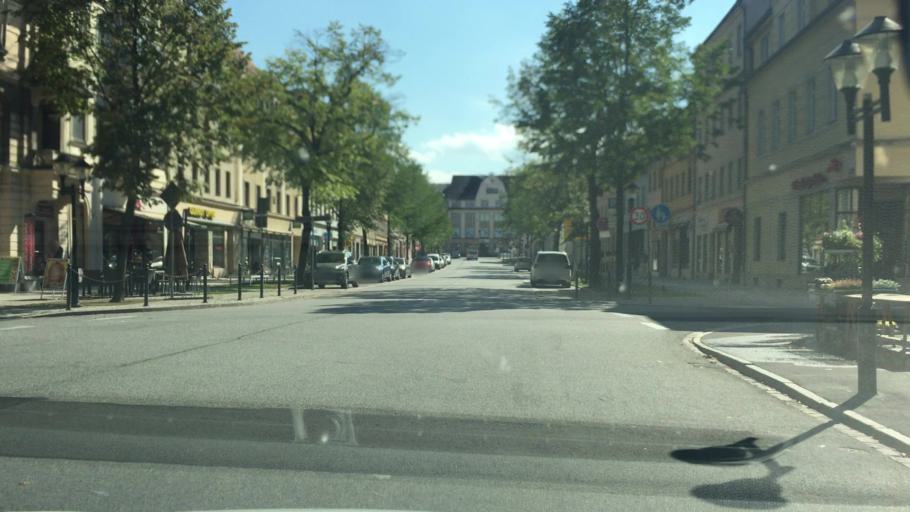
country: DE
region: Saxony
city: Pirna
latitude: 50.9599
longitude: 13.9390
